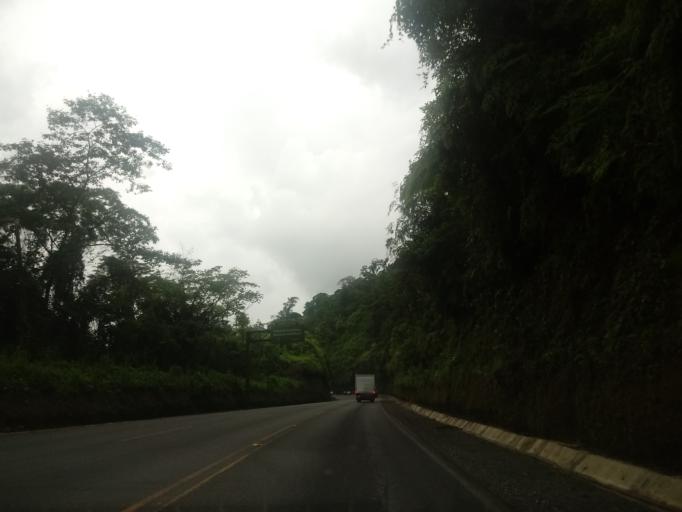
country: CR
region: San Jose
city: Dulce Nombre de Jesus
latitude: 10.1675
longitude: -83.9358
